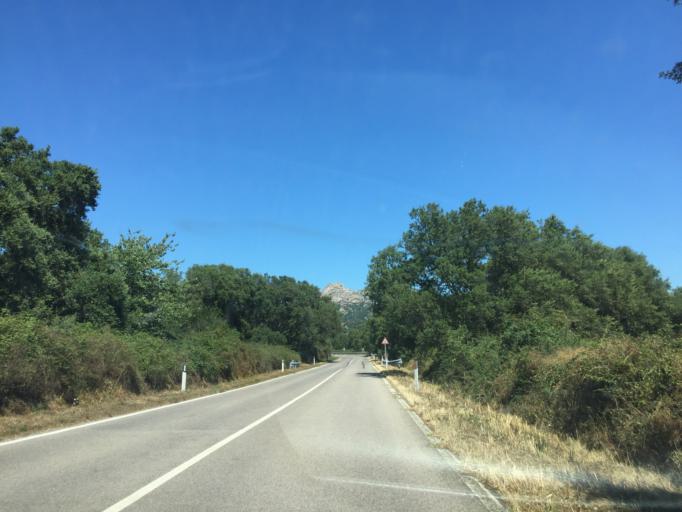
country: IT
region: Sardinia
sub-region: Provincia di Olbia-Tempio
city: Aggius
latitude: 40.9733
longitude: 9.0930
